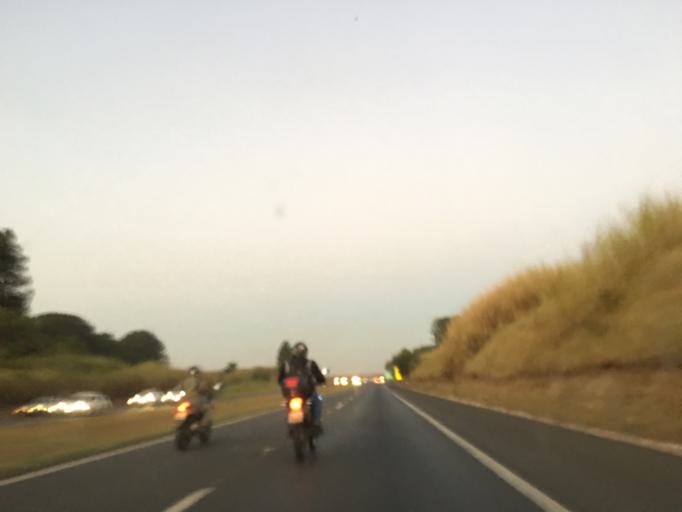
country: BR
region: Sao Paulo
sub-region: Piracicaba
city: Piracicaba
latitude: -22.7211
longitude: -47.6131
